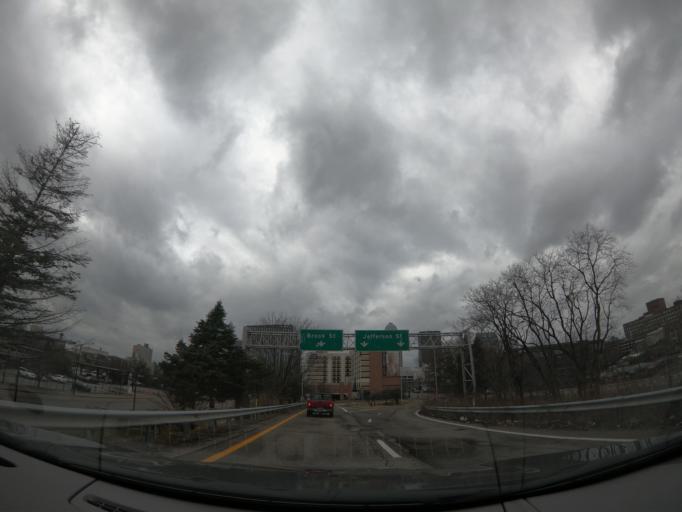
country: US
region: Kentucky
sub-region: Jefferson County
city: Louisville
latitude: 38.2522
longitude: -85.7488
